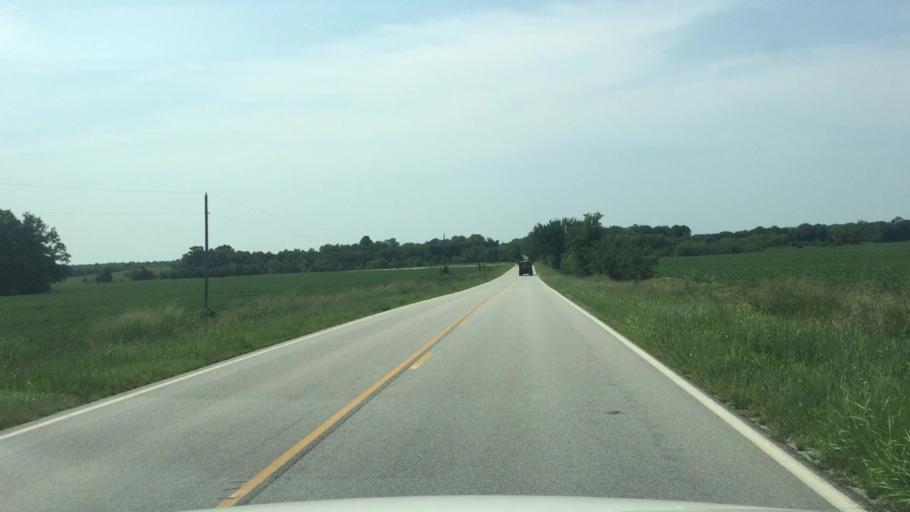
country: US
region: Kansas
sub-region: Montgomery County
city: Cherryvale
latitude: 37.1988
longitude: -95.5579
